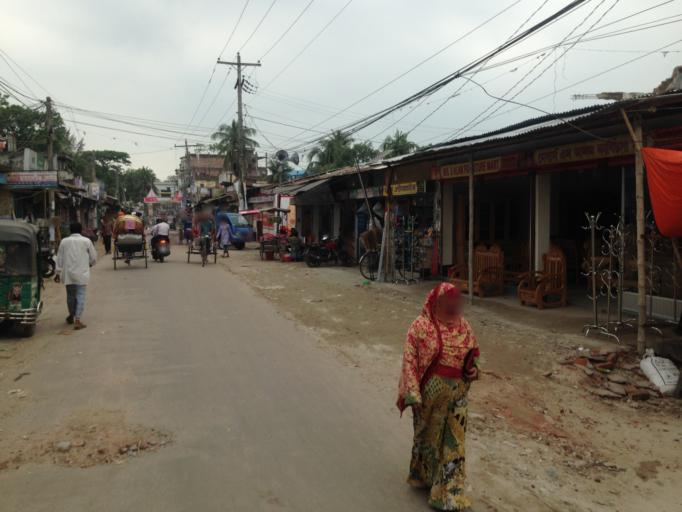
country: BD
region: Chittagong
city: Raipur
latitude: 23.0367
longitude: 90.7653
